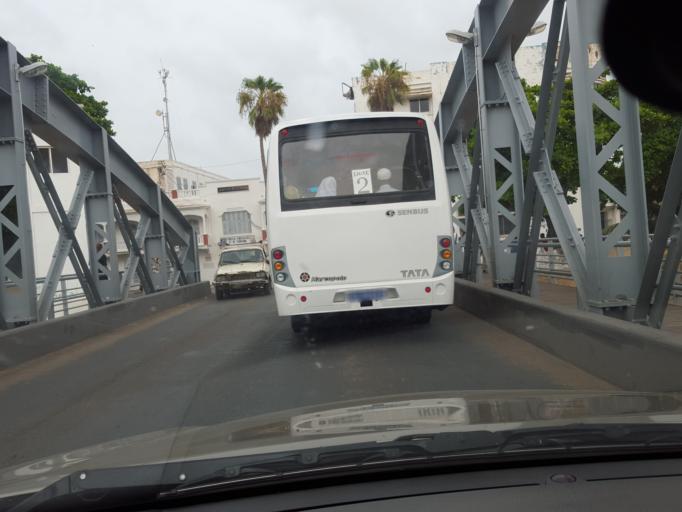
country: SN
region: Saint-Louis
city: Saint-Louis
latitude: 16.0259
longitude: -16.5032
